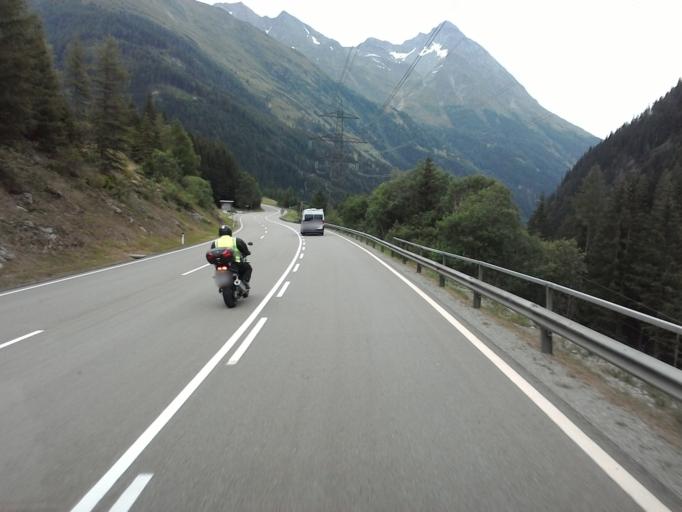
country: AT
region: Tyrol
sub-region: Politischer Bezirk Lienz
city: Matrei in Osttirol
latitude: 47.0932
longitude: 12.5204
